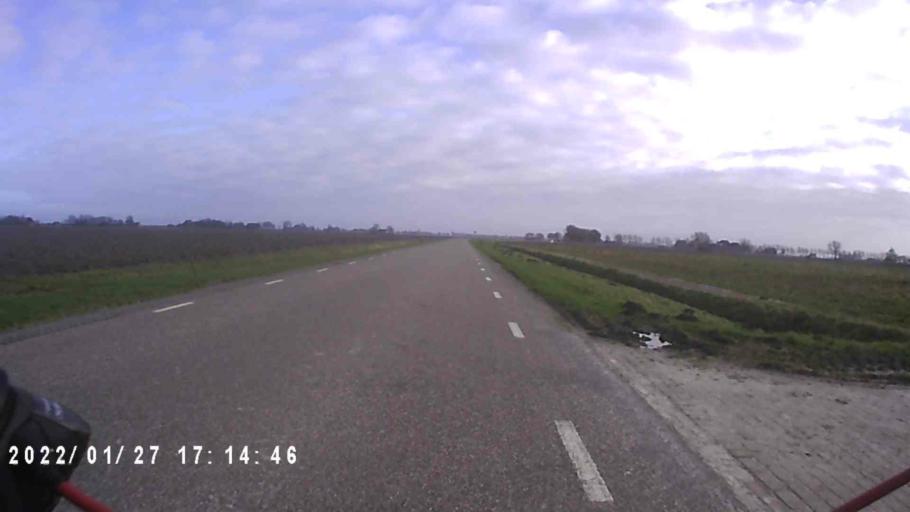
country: NL
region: Friesland
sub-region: Gemeente Dongeradeel
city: Anjum
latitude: 53.3949
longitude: 6.0954
